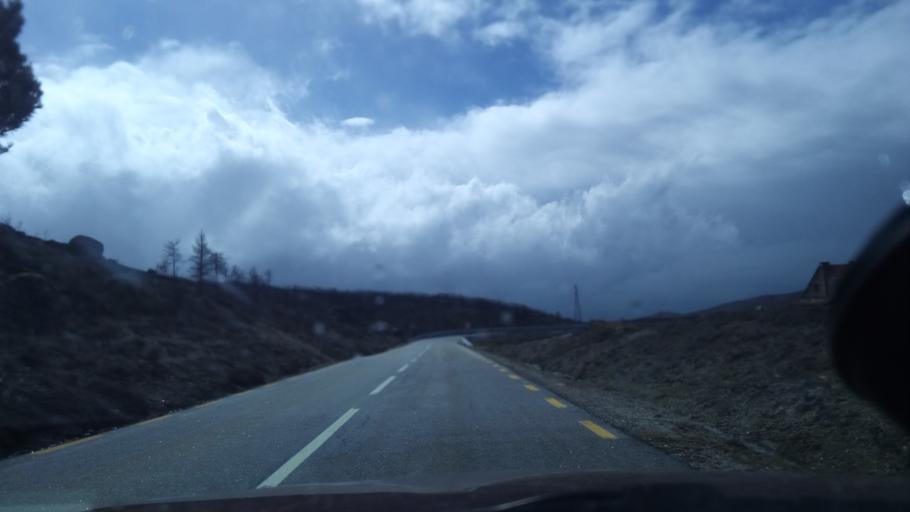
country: PT
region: Guarda
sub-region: Manteigas
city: Manteigas
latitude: 40.4186
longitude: -7.6017
